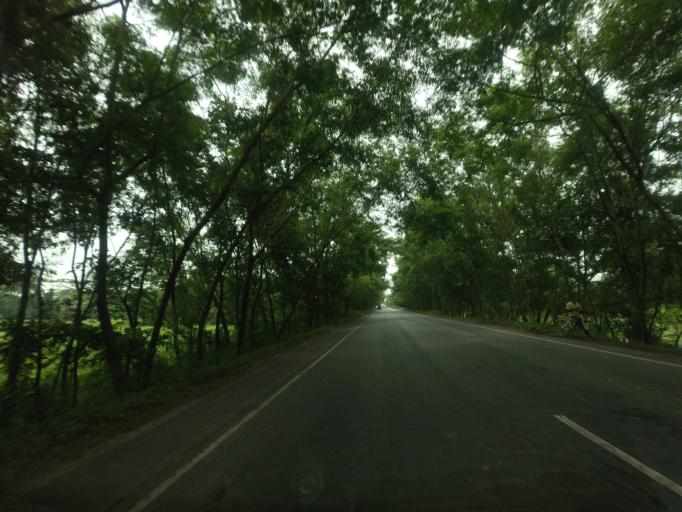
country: BD
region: Khulna
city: Kalia
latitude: 23.2375
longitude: 89.7472
